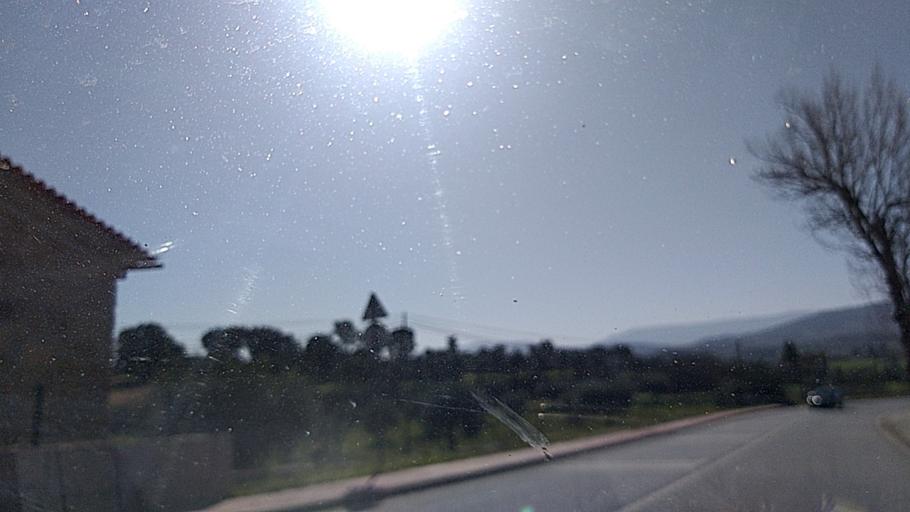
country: PT
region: Guarda
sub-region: Celorico da Beira
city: Celorico da Beira
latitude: 40.6572
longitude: -7.3810
